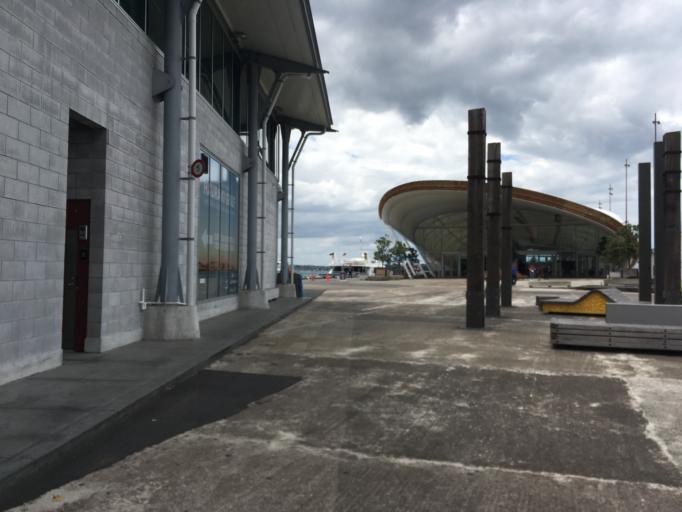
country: NZ
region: Auckland
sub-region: Auckland
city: Auckland
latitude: -36.8423
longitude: 174.7675
